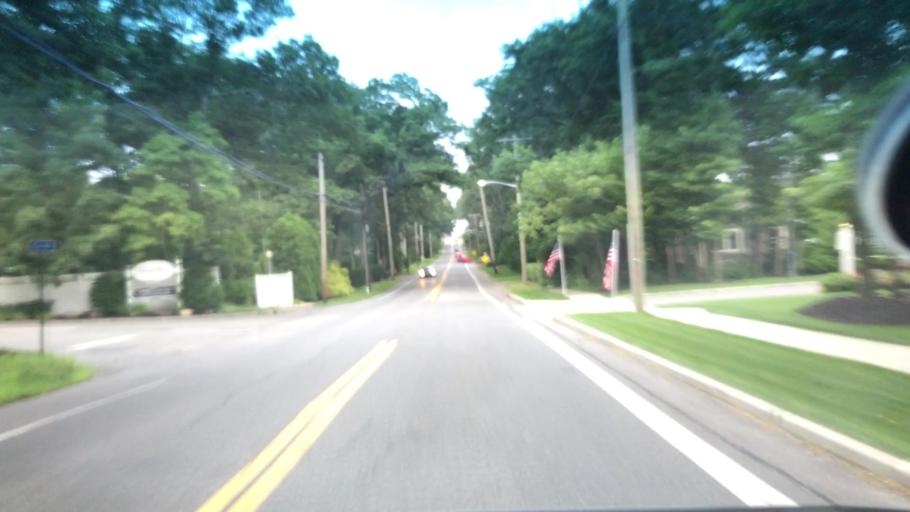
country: US
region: New York
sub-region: Suffolk County
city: Wading River
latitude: 40.9460
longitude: -72.8202
